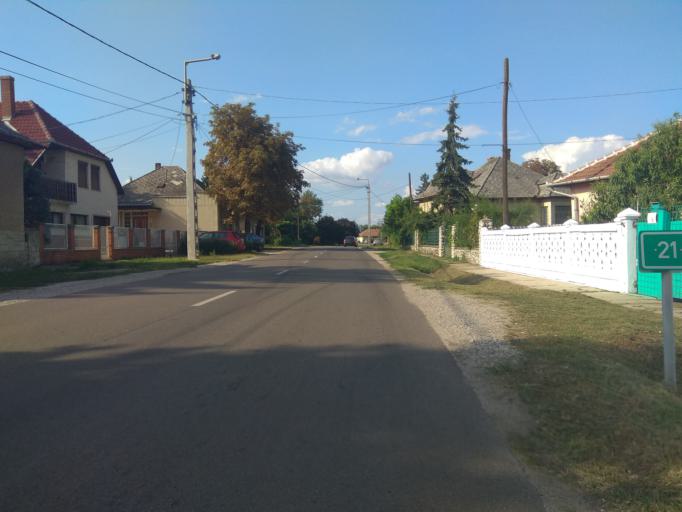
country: HU
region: Borsod-Abauj-Zemplen
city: Mezocsat
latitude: 47.8272
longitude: 20.9022
